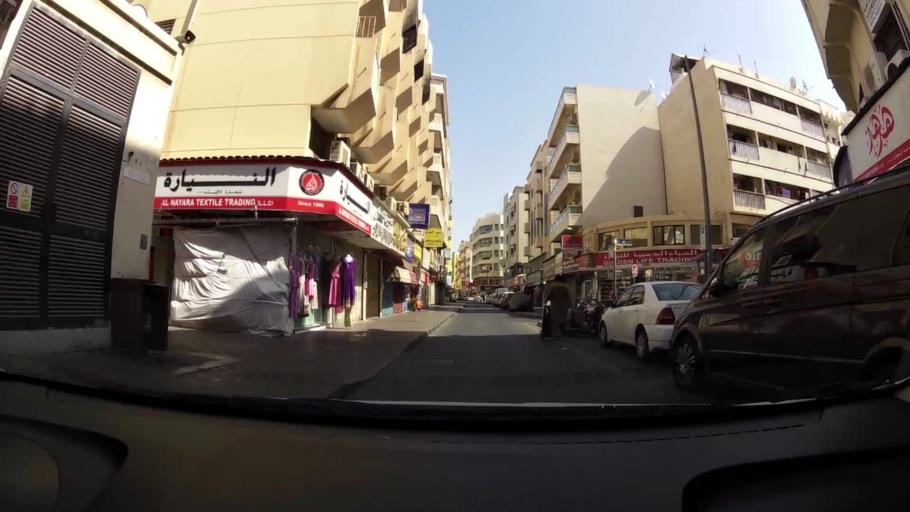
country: AE
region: Ash Shariqah
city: Sharjah
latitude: 25.2714
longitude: 55.3003
